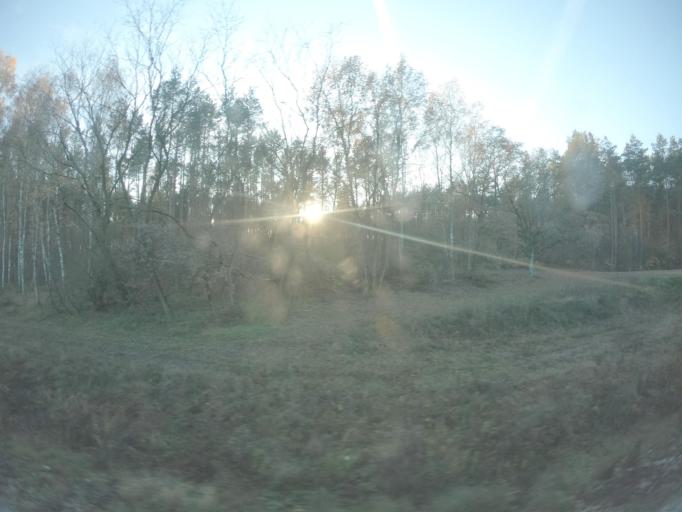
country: PL
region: Lubusz
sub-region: Powiat slubicki
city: Rzepin
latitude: 52.3316
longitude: 14.8378
